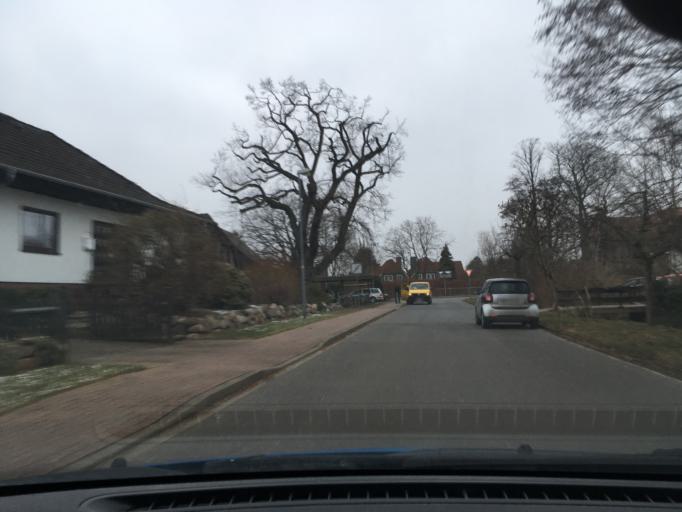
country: DE
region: Lower Saxony
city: Stelle
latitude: 53.3654
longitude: 10.1436
